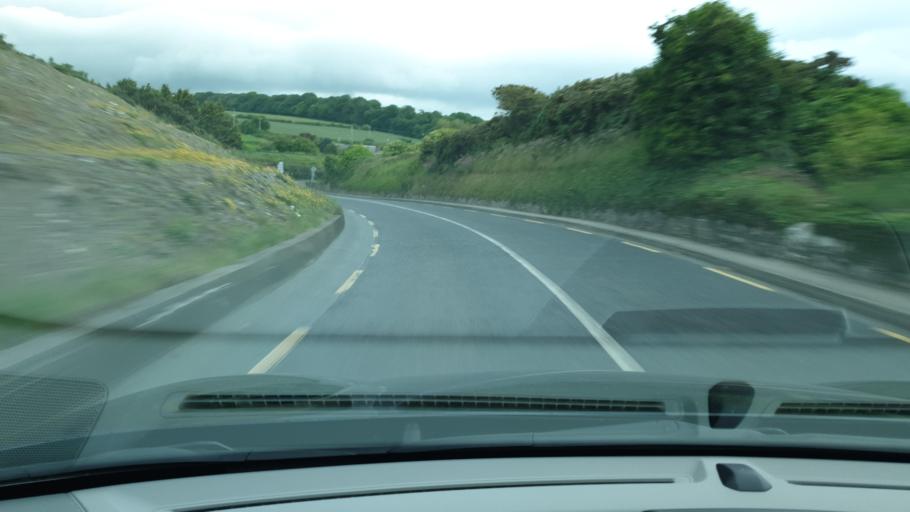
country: IE
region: Leinster
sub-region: Fingal County
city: Skerries
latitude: 53.5856
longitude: -6.1464
